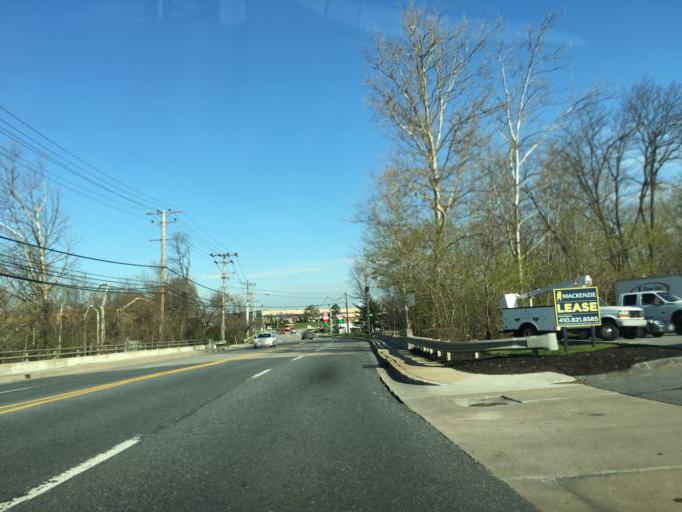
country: US
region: Maryland
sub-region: Baltimore County
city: Cockeysville
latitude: 39.4793
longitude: -76.6544
